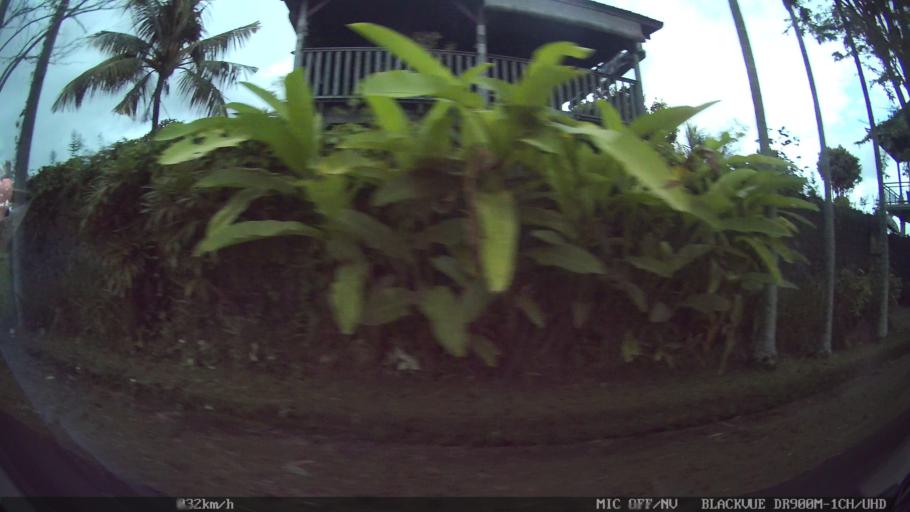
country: ID
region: Bali
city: Banjar Cemenggon
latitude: -8.5300
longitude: 115.1944
